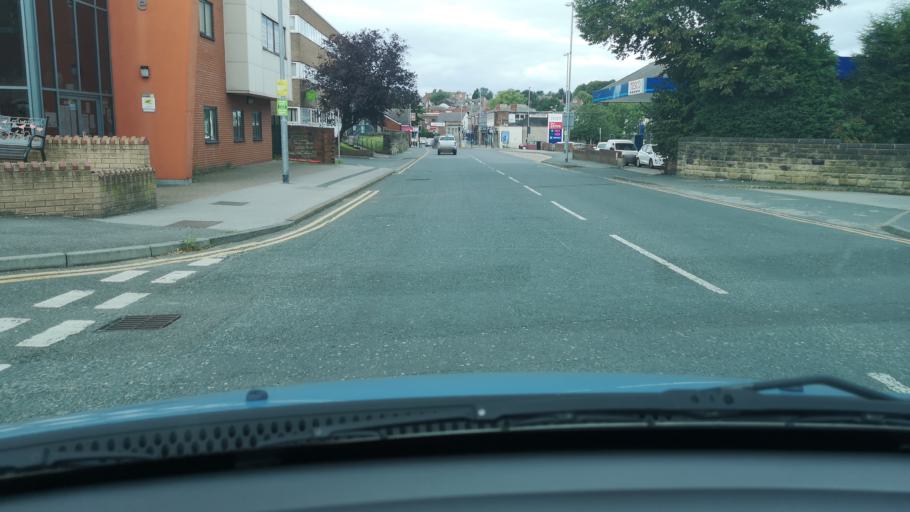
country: GB
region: England
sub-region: City and Borough of Wakefield
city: Hemsworth
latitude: 53.6111
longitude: -1.3525
